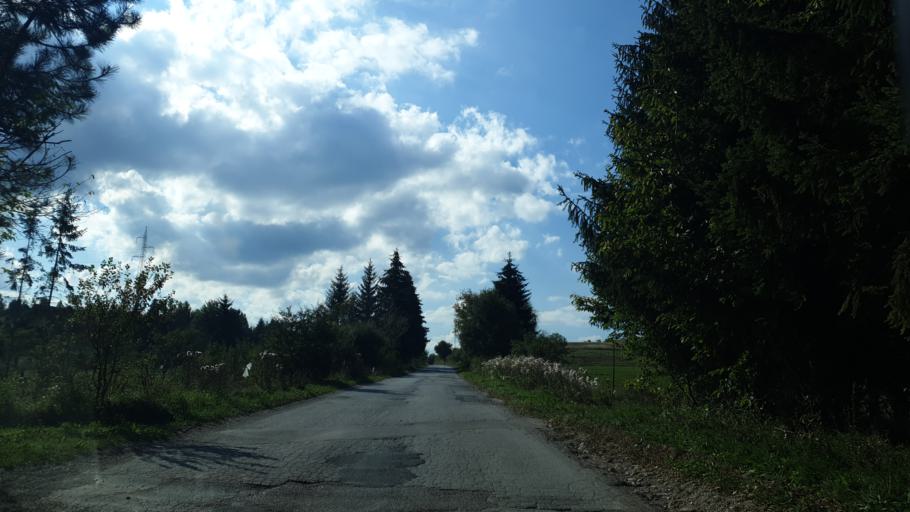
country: RS
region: Central Serbia
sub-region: Zlatiborski Okrug
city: Nova Varos
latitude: 43.4255
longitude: 19.9109
